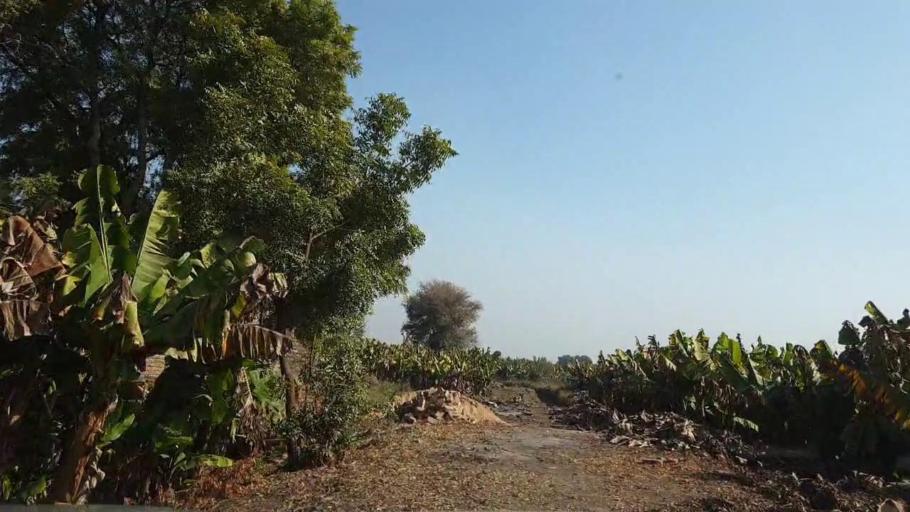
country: PK
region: Sindh
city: Tando Allahyar
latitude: 25.5142
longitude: 68.6897
